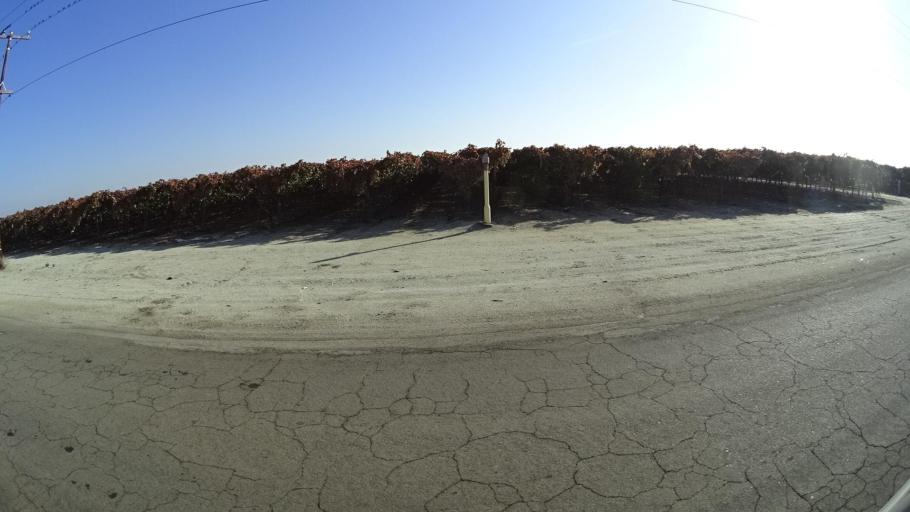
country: US
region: California
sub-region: Kern County
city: McFarland
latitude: 35.7220
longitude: -119.1694
